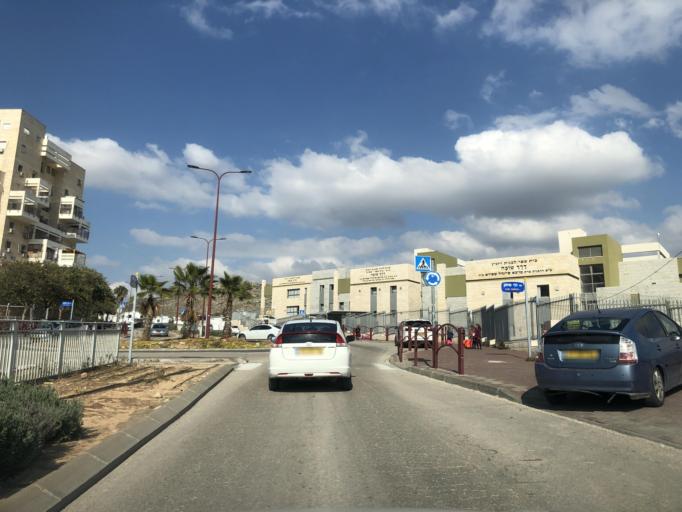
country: IL
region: Jerusalem
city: Modiin Ilit
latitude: 31.9373
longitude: 35.0471
